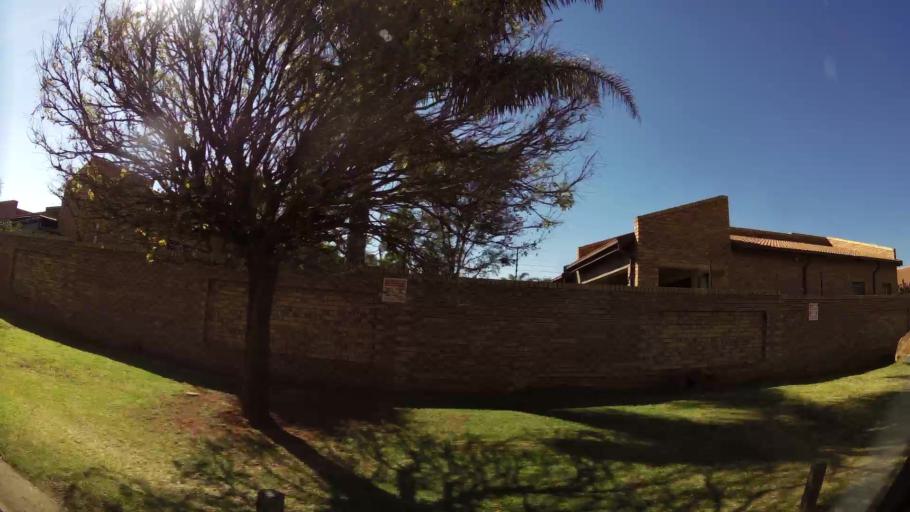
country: ZA
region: Gauteng
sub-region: Ekurhuleni Metropolitan Municipality
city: Germiston
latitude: -26.2977
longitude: 28.0958
